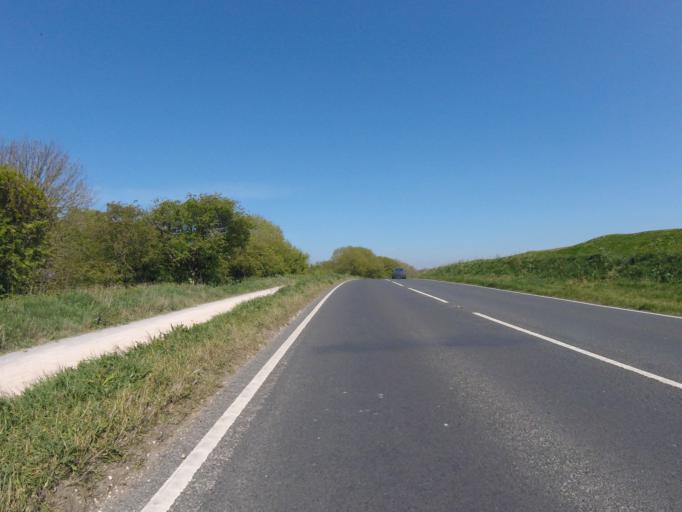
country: GB
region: England
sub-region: Brighton and Hove
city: Brighton
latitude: 50.8574
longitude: -0.1294
